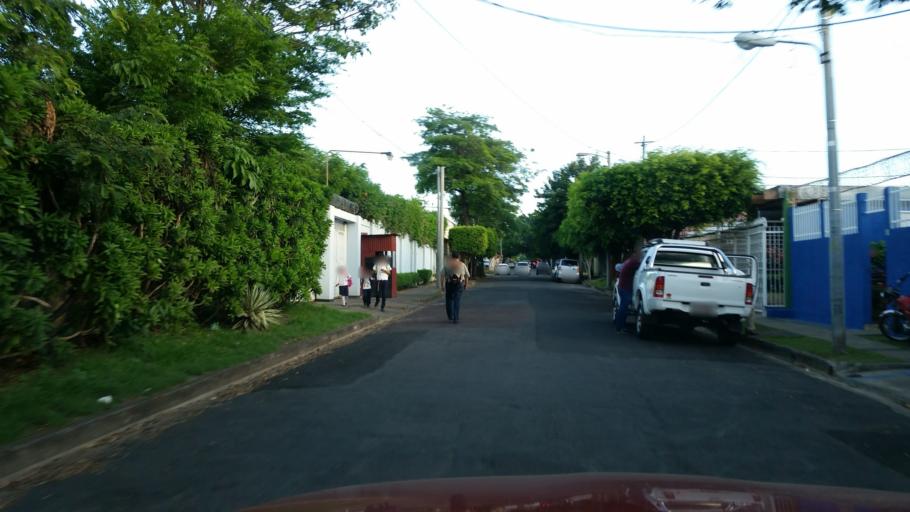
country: NI
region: Managua
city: Managua
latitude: 12.1393
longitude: -86.2864
